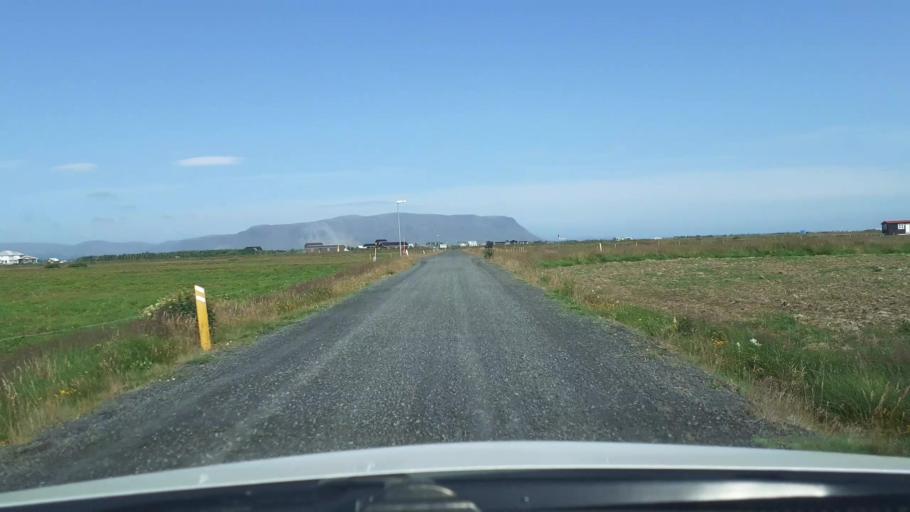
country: IS
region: South
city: Selfoss
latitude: 63.8869
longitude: -21.0913
